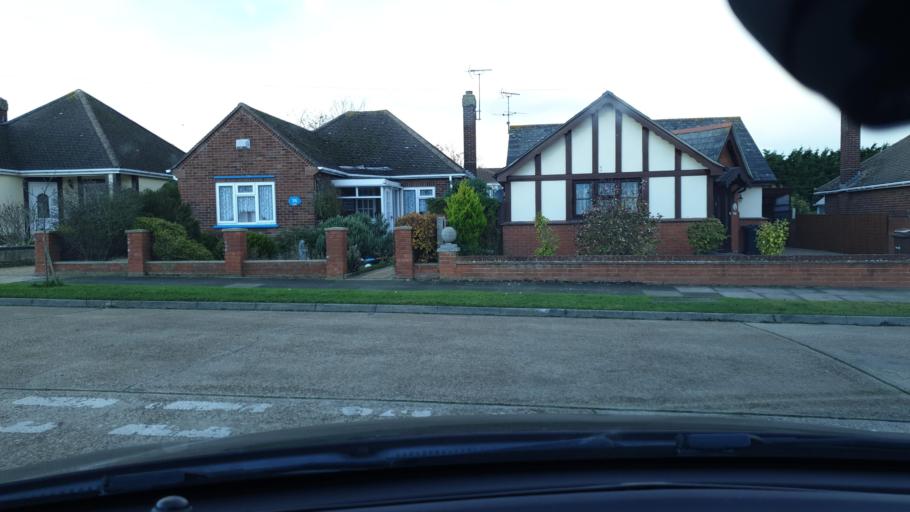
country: GB
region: England
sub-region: Essex
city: Clacton-on-Sea
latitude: 51.8018
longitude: 1.1676
